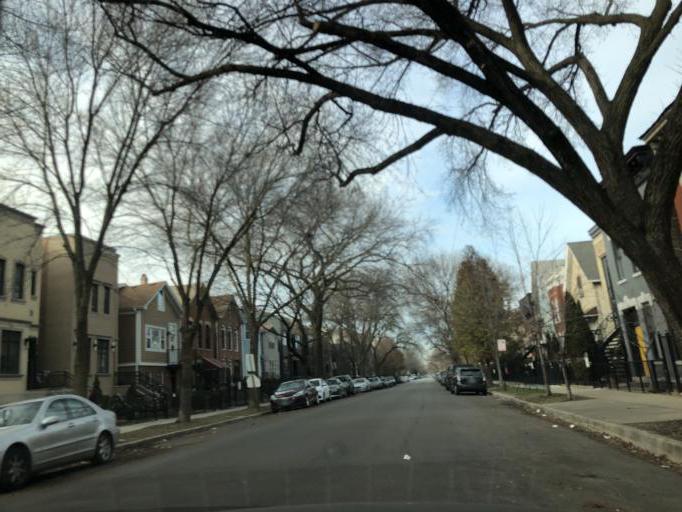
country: US
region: Illinois
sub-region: Cook County
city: Chicago
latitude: 41.8932
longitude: -87.6746
